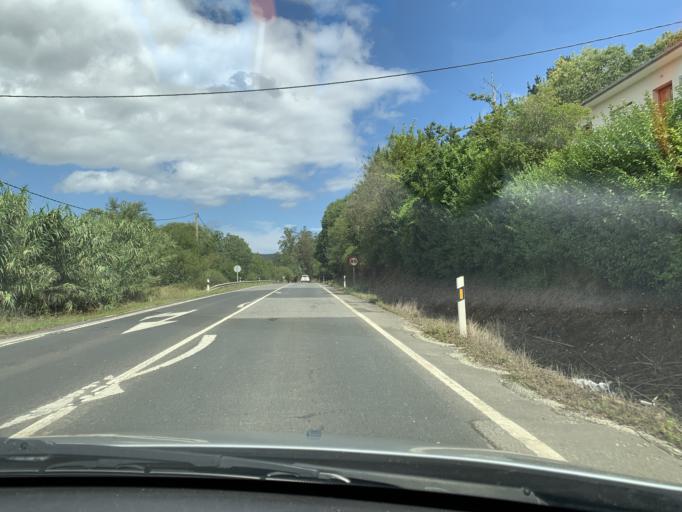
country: ES
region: Galicia
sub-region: Provincia de Lugo
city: Barreiros
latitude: 43.4877
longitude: -7.2881
